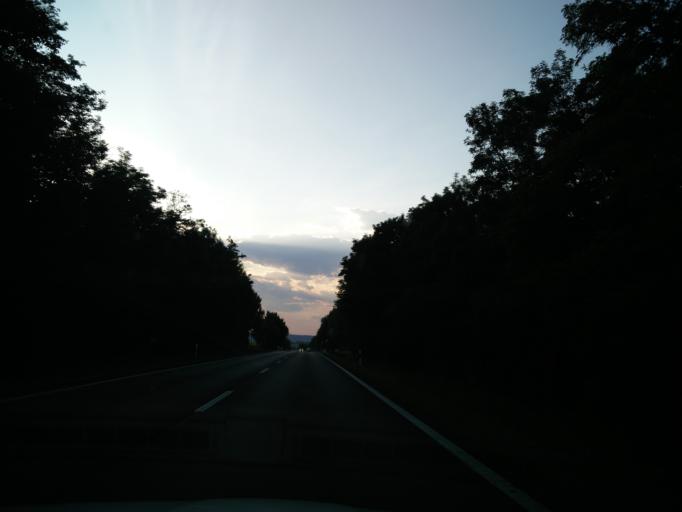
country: HU
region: Vas
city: Janoshaza
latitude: 47.1128
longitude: 17.1556
